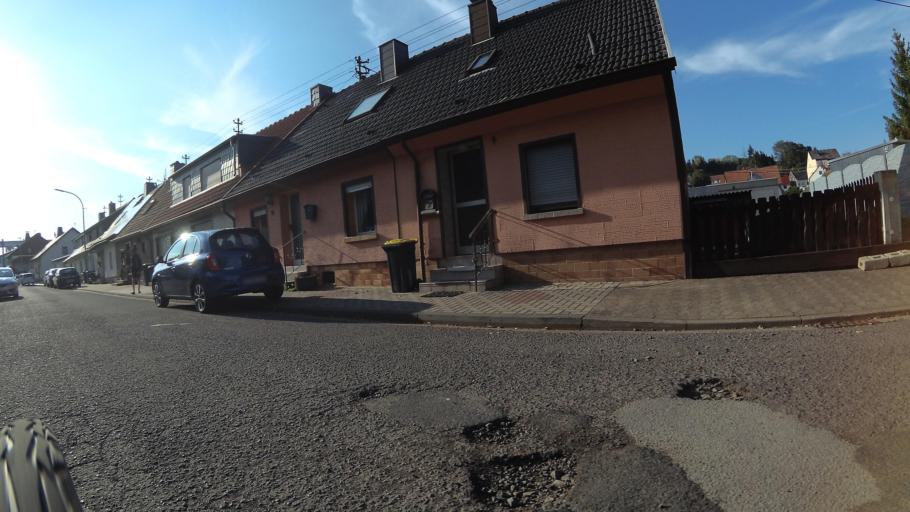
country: DE
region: Saarland
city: Friedrichsthal
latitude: 49.3179
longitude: 7.0928
